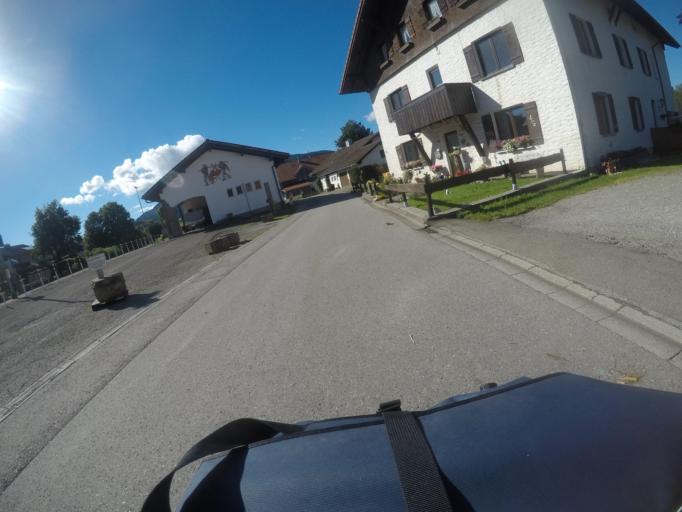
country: DE
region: Bavaria
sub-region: Swabia
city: Oy-Mittelberg
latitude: 47.6289
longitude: 10.4600
